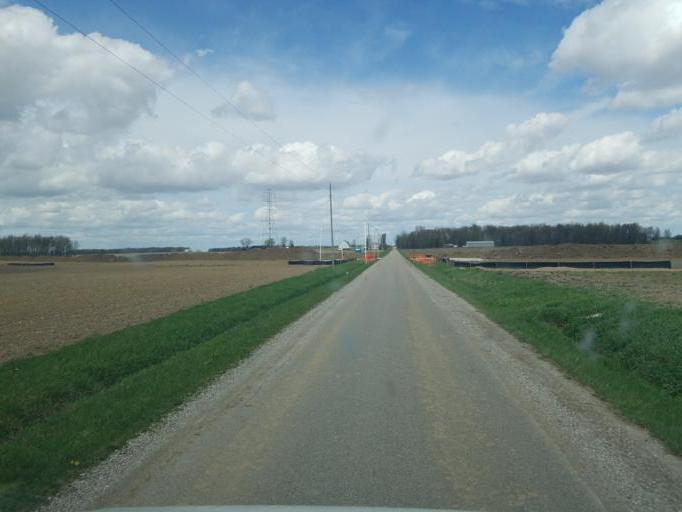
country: US
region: Ohio
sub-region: Crawford County
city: Bucyrus
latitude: 40.9375
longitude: -82.8825
